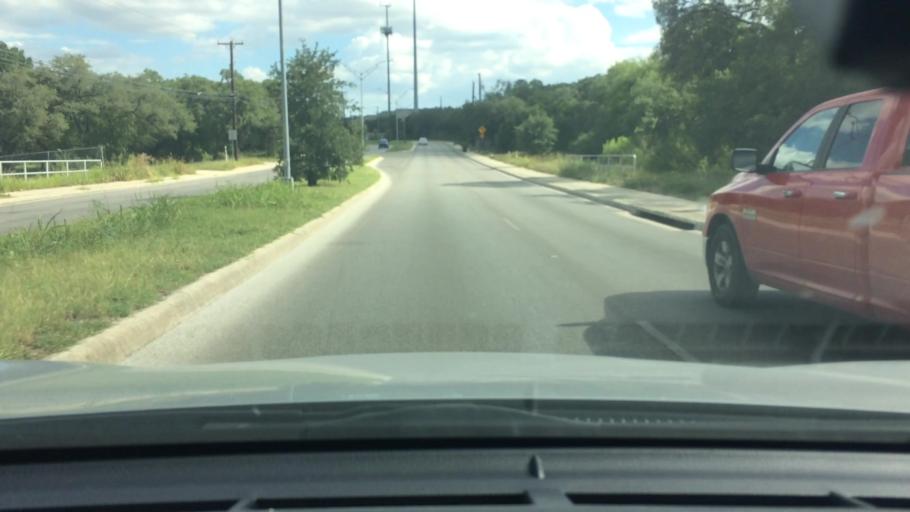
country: US
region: Texas
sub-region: Bexar County
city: Leon Valley
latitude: 29.4847
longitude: -98.7003
